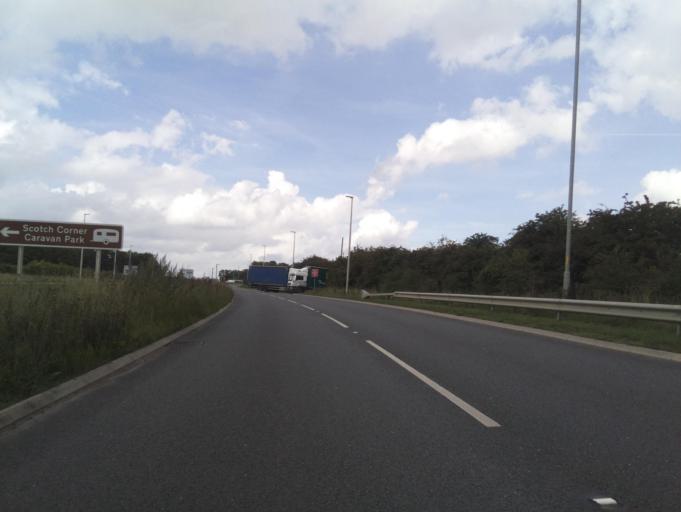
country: GB
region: England
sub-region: North Yorkshire
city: Catterick
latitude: 54.4391
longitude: -1.6701
